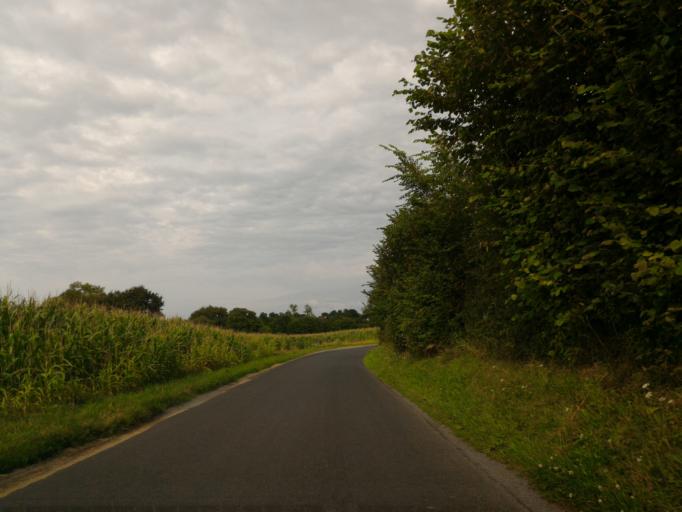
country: FR
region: Lower Normandy
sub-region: Departement de la Manche
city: Jullouville
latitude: 48.7812
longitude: -1.5249
